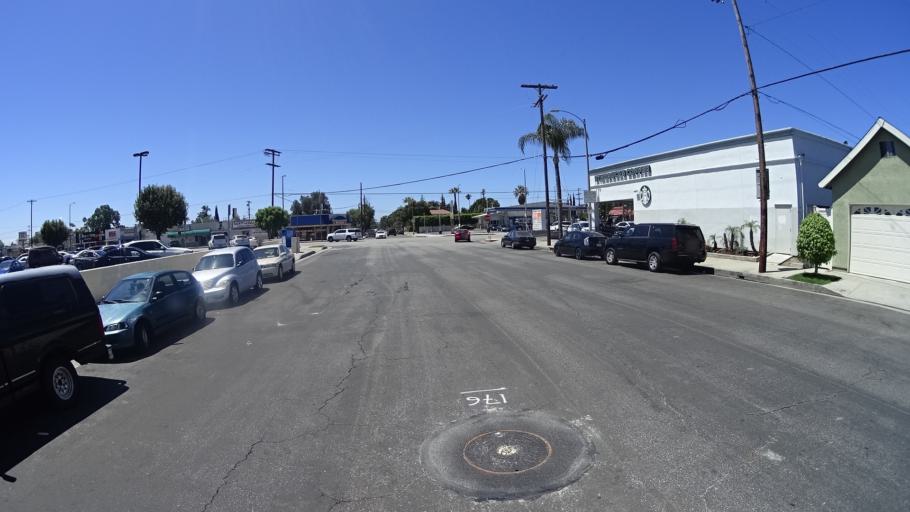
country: US
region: California
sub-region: Los Angeles County
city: San Fernando
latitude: 34.2580
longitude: -118.4696
